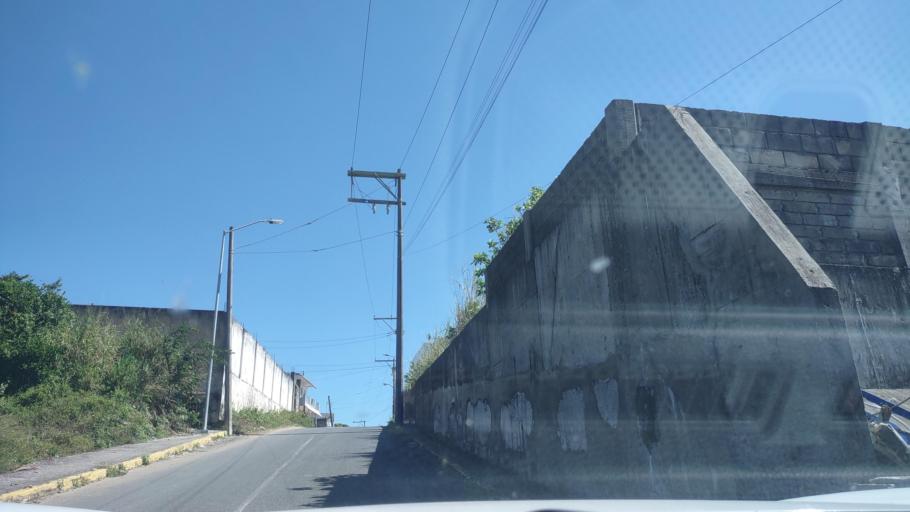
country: MX
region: Veracruz
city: Heroica Alvarado
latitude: 18.7772
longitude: -95.7595
